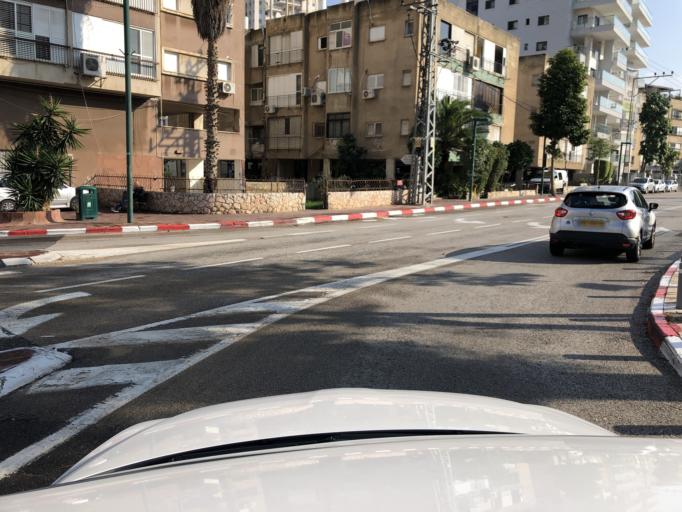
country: IL
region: Tel Aviv
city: Ramat Gan
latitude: 32.0901
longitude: 34.8201
